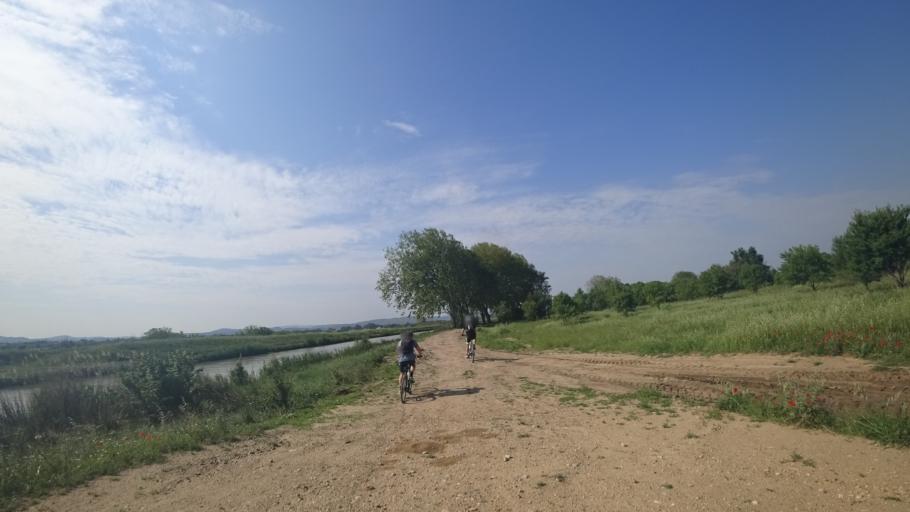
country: FR
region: Languedoc-Roussillon
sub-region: Departement de l'Aude
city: Ginestas
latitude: 43.2555
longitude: 2.8862
